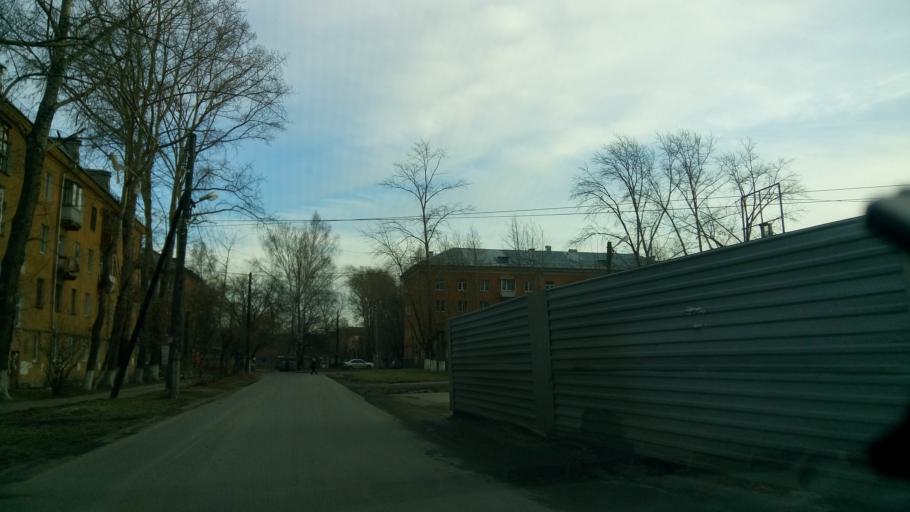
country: RU
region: Sverdlovsk
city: Shuvakish
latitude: 56.8734
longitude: 60.5251
